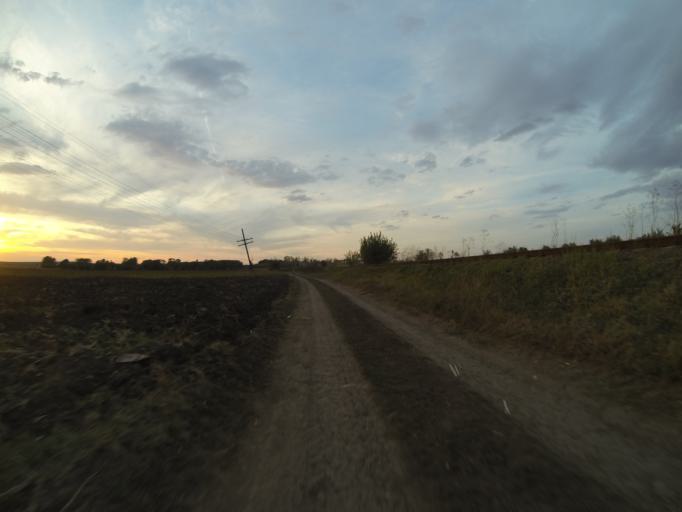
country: RO
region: Dolj
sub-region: Comuna Segarcea
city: Segarcea
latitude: 44.0988
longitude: 23.7241
